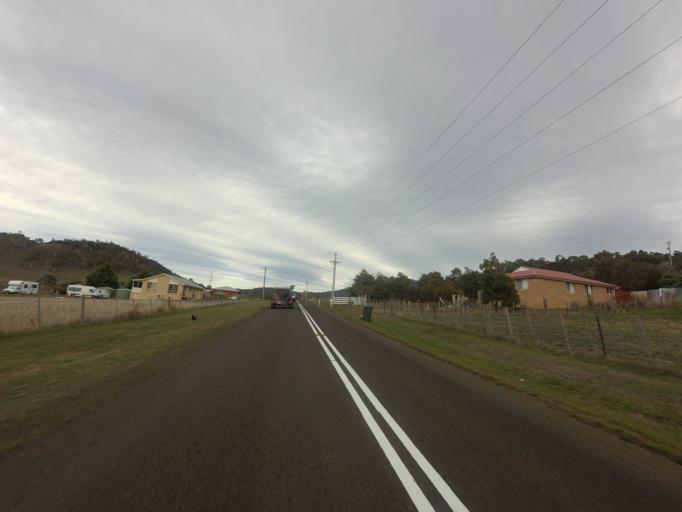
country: AU
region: Tasmania
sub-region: Brighton
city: Bridgewater
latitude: -42.6538
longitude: 147.1253
